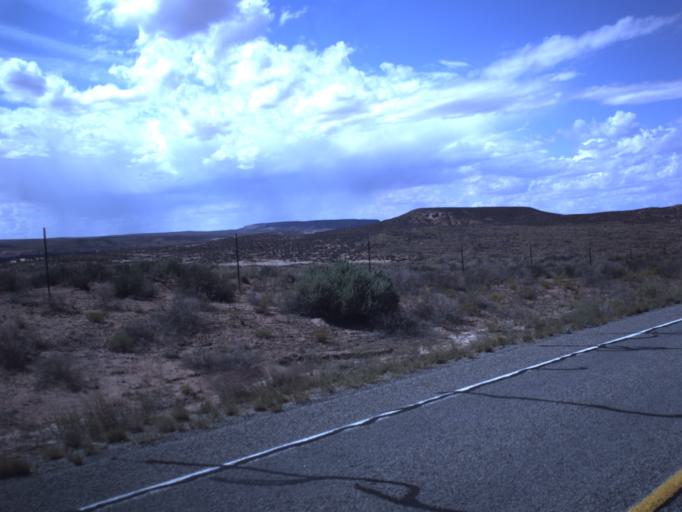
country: US
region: Utah
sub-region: San Juan County
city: Blanding
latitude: 37.2978
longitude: -109.4707
